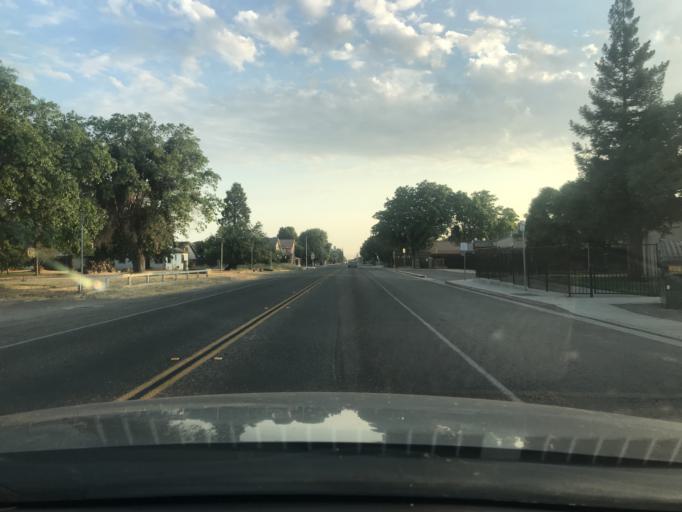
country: US
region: California
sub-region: Merced County
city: Merced
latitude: 37.3271
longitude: -120.5409
